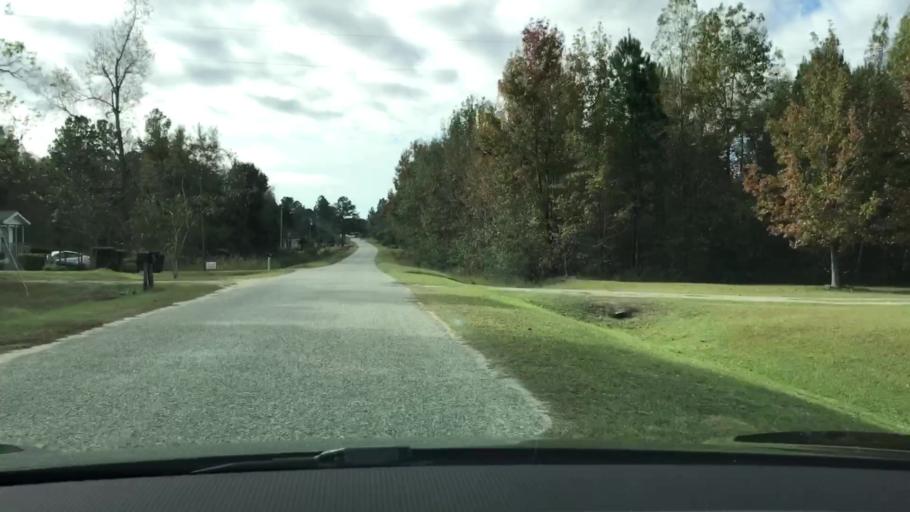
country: US
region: Georgia
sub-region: Jefferson County
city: Wadley
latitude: 32.8051
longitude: -82.3453
